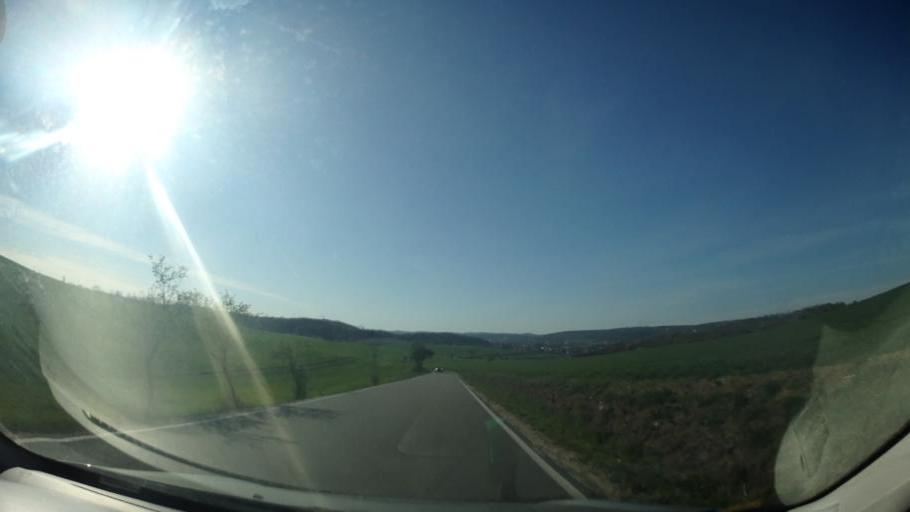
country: CZ
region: South Moravian
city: Moravany
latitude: 49.1494
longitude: 16.5642
